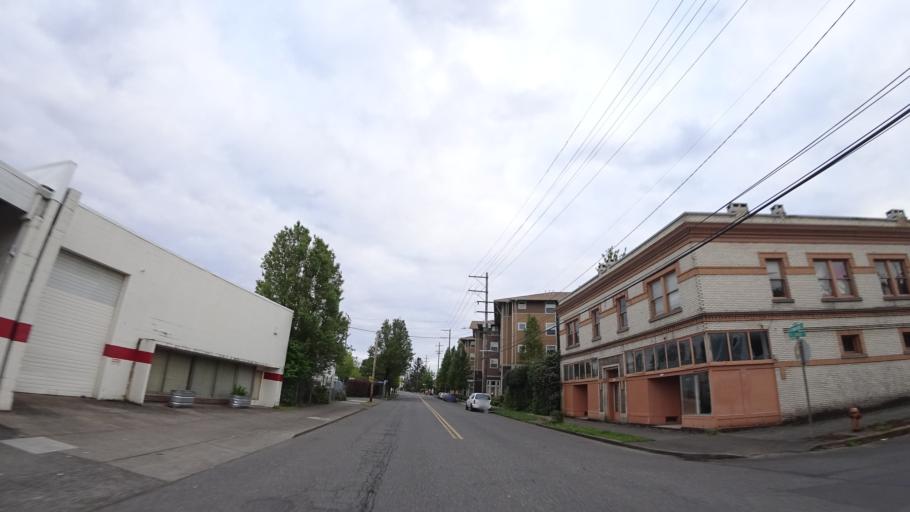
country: US
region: Oregon
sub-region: Multnomah County
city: Portland
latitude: 45.4950
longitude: -122.6531
